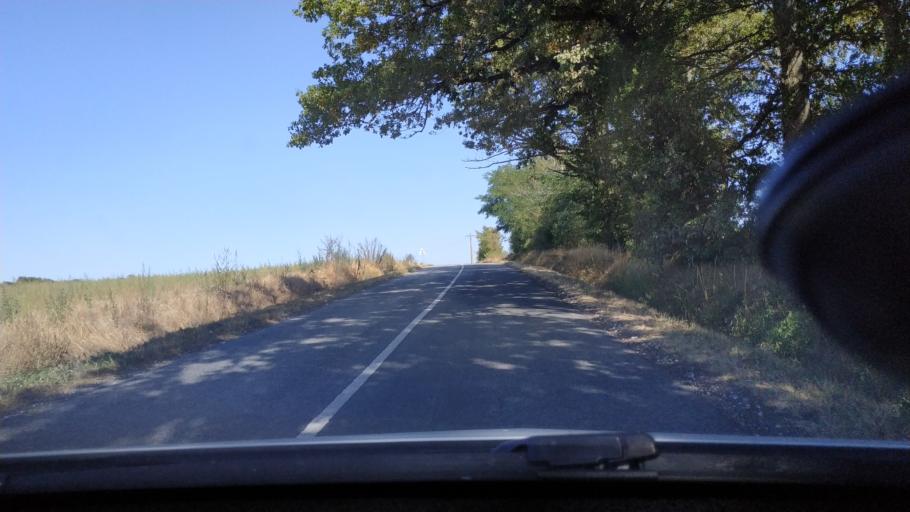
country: FR
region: Centre
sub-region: Departement du Loiret
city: Coullons
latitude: 47.6255
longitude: 2.5032
